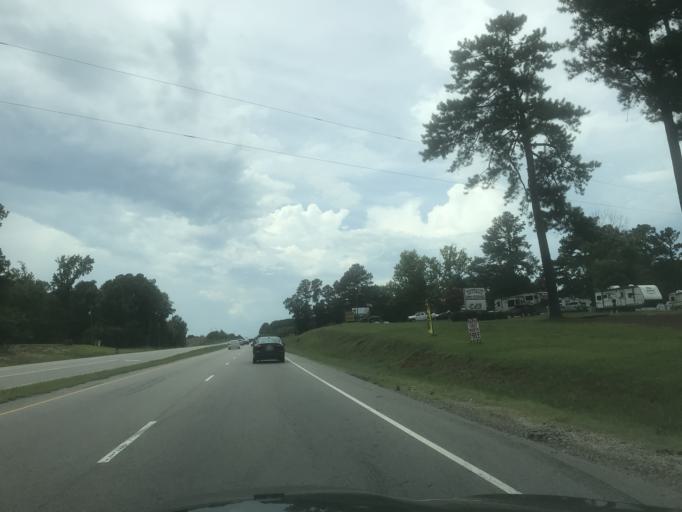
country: US
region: North Carolina
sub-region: Wake County
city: Garner
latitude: 35.6846
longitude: -78.5406
